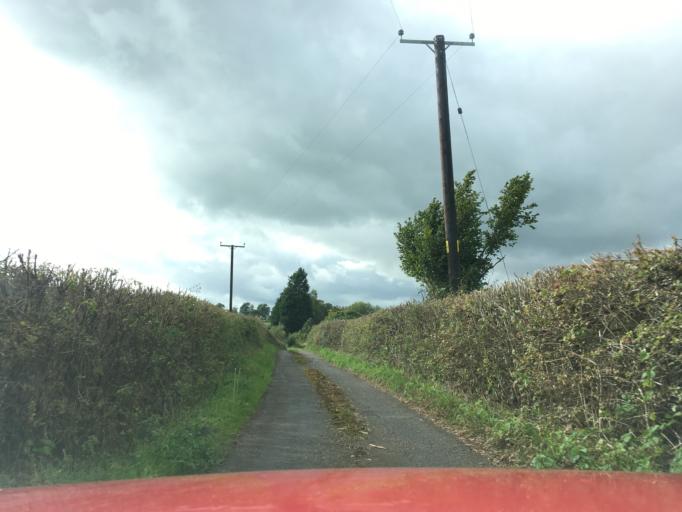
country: GB
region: England
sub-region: South Gloucestershire
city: Falfield
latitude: 51.6272
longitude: -2.4553
